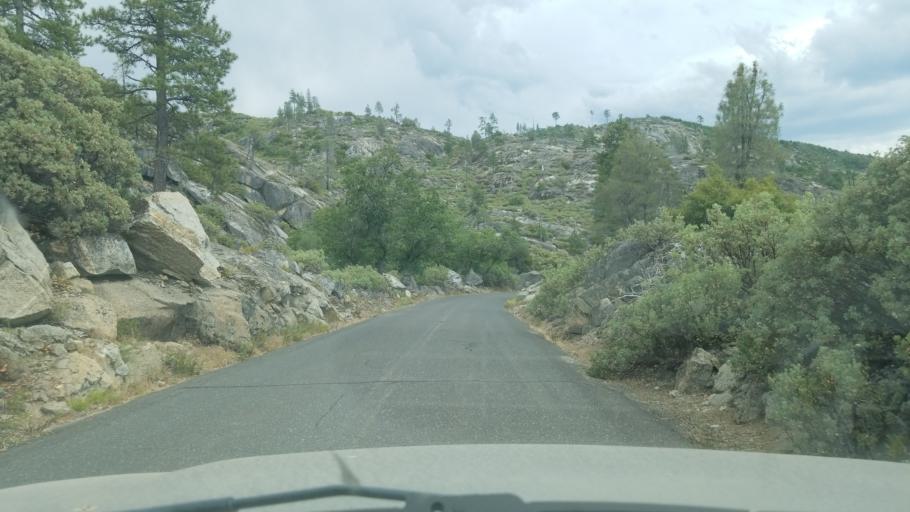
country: US
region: California
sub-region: Mariposa County
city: Yosemite Valley
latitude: 37.9013
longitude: -119.8366
